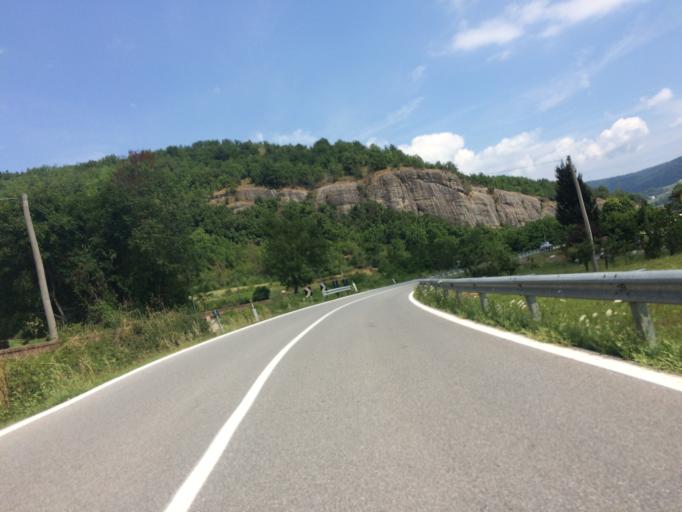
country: IT
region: Piedmont
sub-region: Provincia di Cuneo
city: Bagnasco
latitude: 44.2933
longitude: 8.0358
